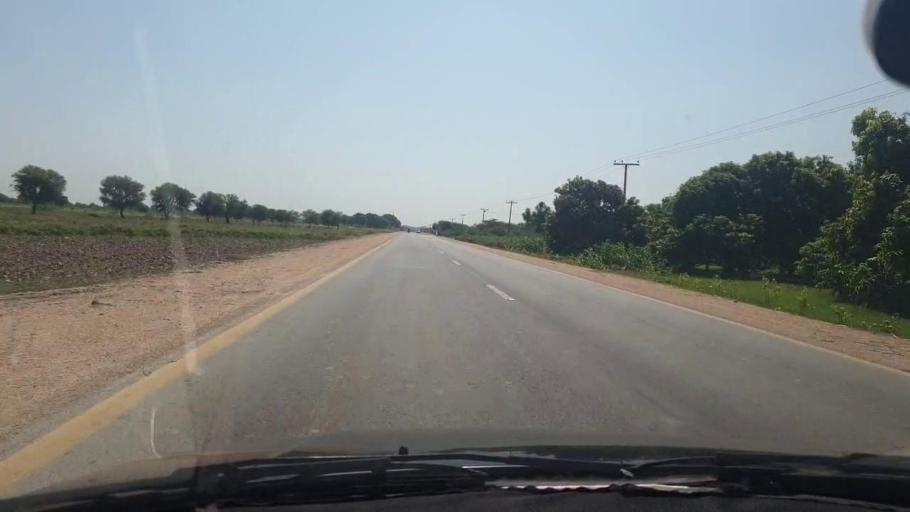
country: PK
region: Sindh
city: Chambar
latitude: 25.3190
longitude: 68.8030
